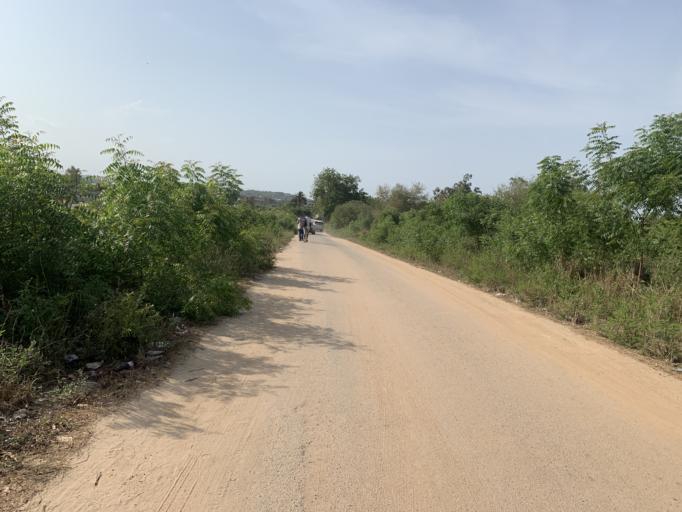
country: GH
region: Central
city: Winneba
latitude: 5.3663
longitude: -0.6465
